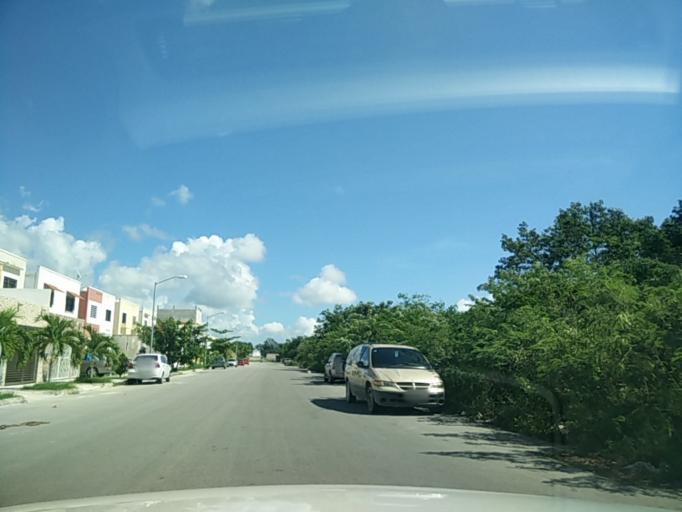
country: MX
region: Quintana Roo
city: Playa del Carmen
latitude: 20.6587
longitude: -87.0640
